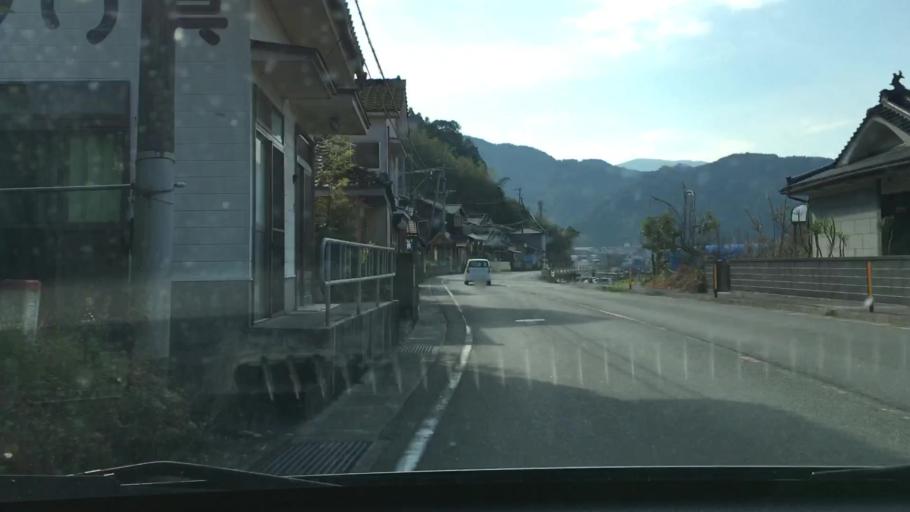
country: JP
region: Kagoshima
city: Hamanoichi
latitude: 31.6178
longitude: 130.7962
